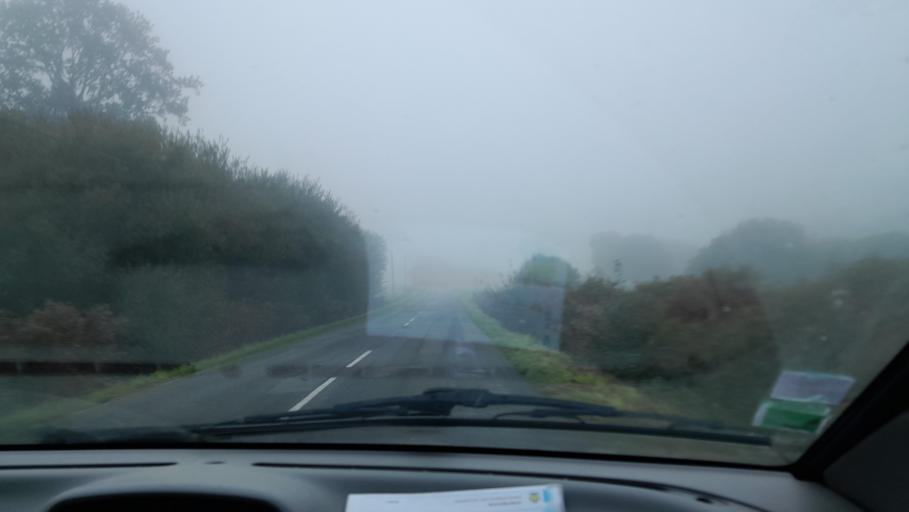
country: FR
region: Brittany
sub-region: Departement d'Ille-et-Vilaine
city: Le Pertre
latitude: 48.0520
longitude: -1.0340
